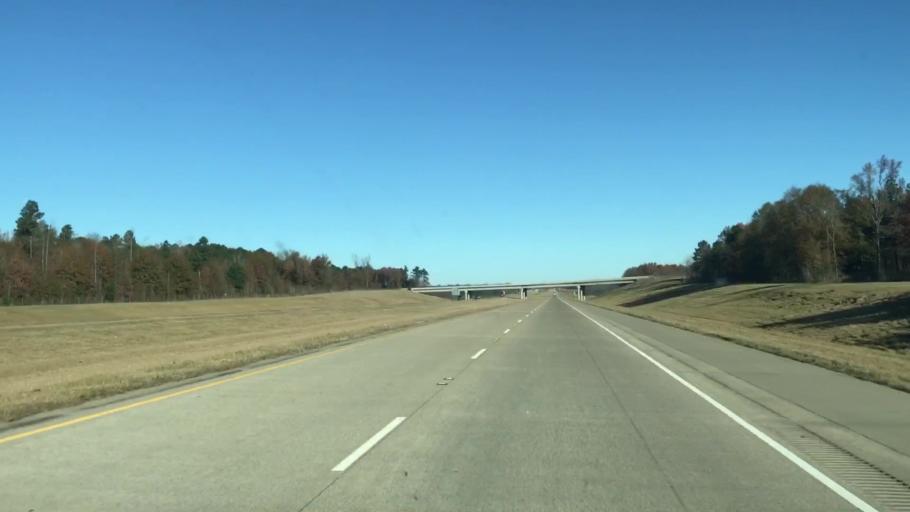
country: US
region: Louisiana
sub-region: Caddo Parish
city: Blanchard
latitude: 32.6124
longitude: -93.8348
